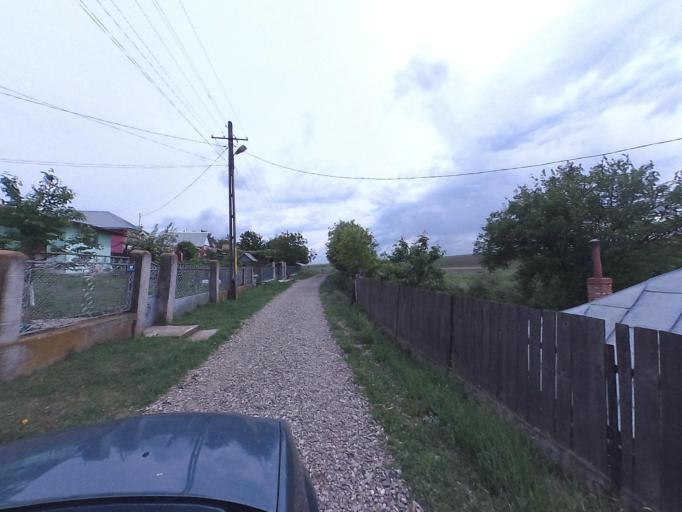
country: RO
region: Neamt
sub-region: Comuna Trifesti
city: Miron Costin
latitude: 46.9542
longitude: 26.7998
